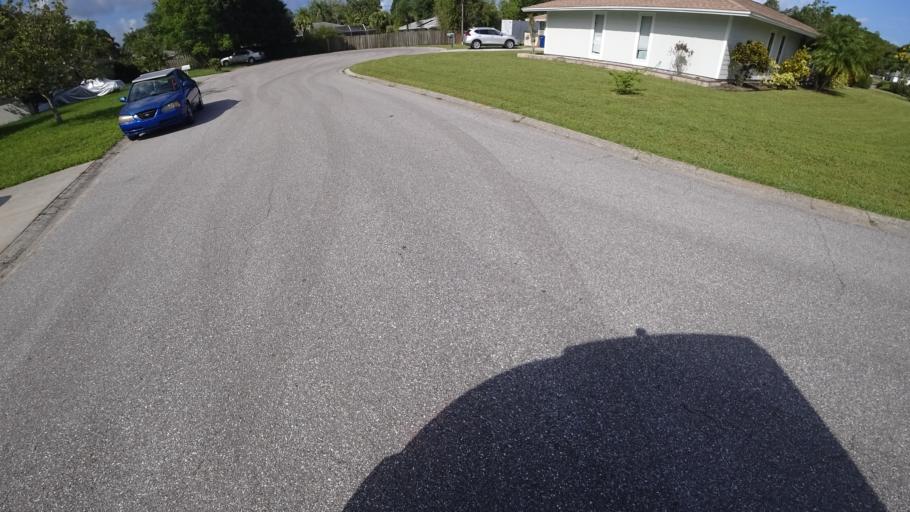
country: US
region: Florida
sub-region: Sarasota County
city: Desoto Lakes
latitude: 27.4032
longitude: -82.4960
